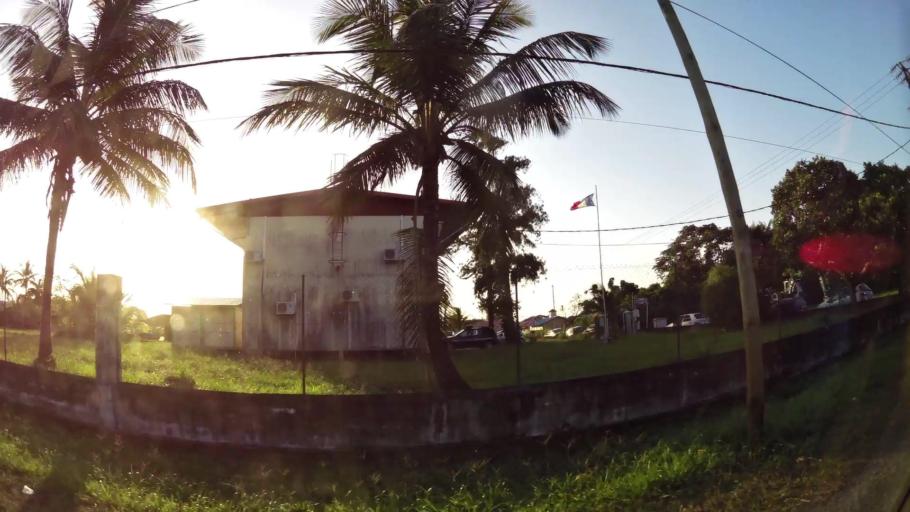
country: GF
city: Macouria
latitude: 5.0116
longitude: -52.4724
